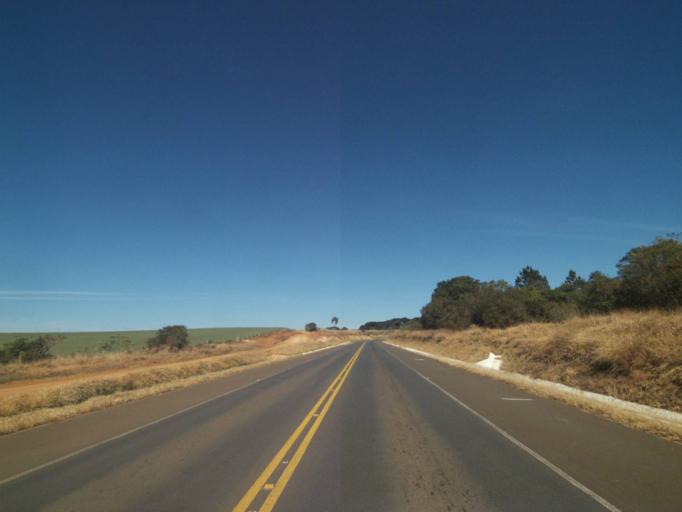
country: BR
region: Parana
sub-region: Tibagi
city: Tibagi
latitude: -24.6910
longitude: -50.4403
